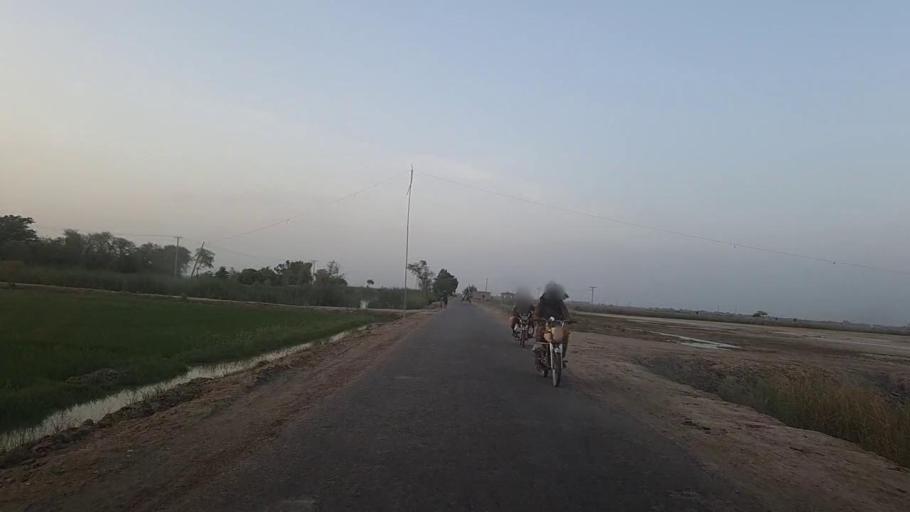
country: PK
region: Sindh
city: Radhan
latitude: 27.1413
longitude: 67.9347
